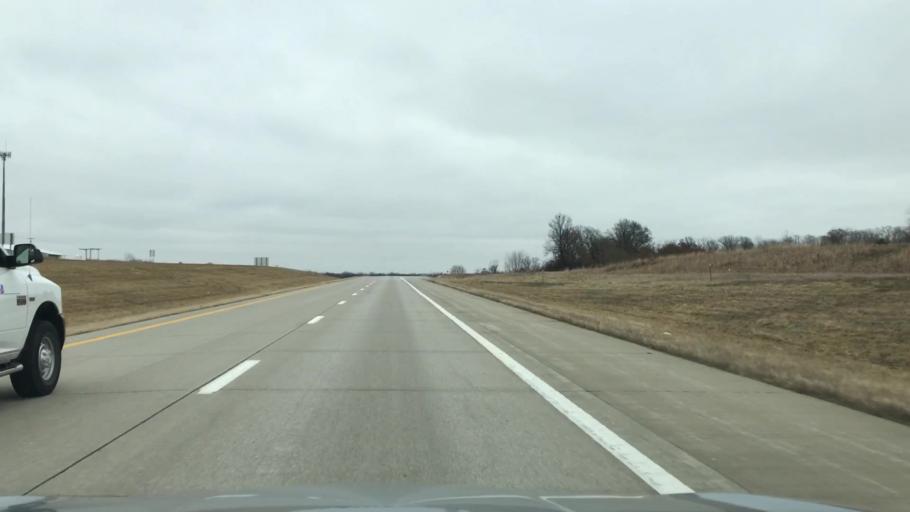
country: US
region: Missouri
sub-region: Linn County
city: Marceline
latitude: 39.7651
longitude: -92.7461
